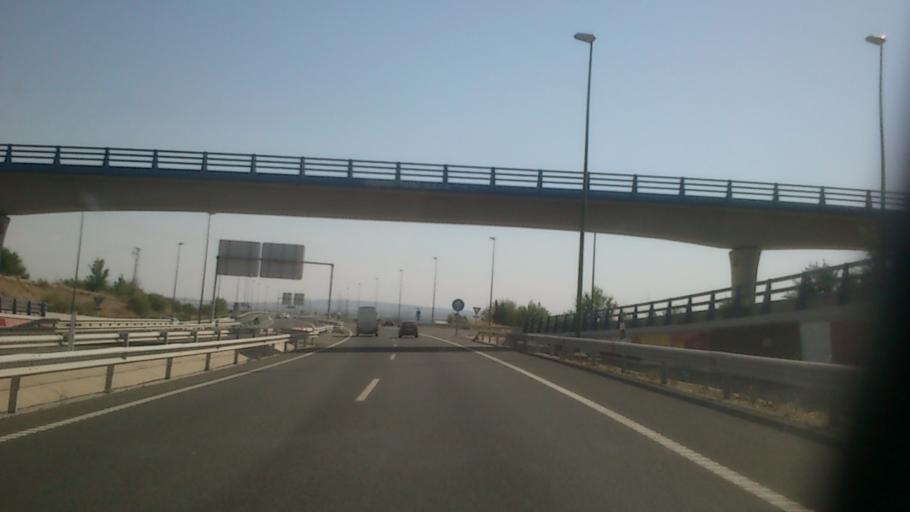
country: ES
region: Aragon
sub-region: Provincia de Zaragoza
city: Zaragoza
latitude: 41.6647
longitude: -0.8387
